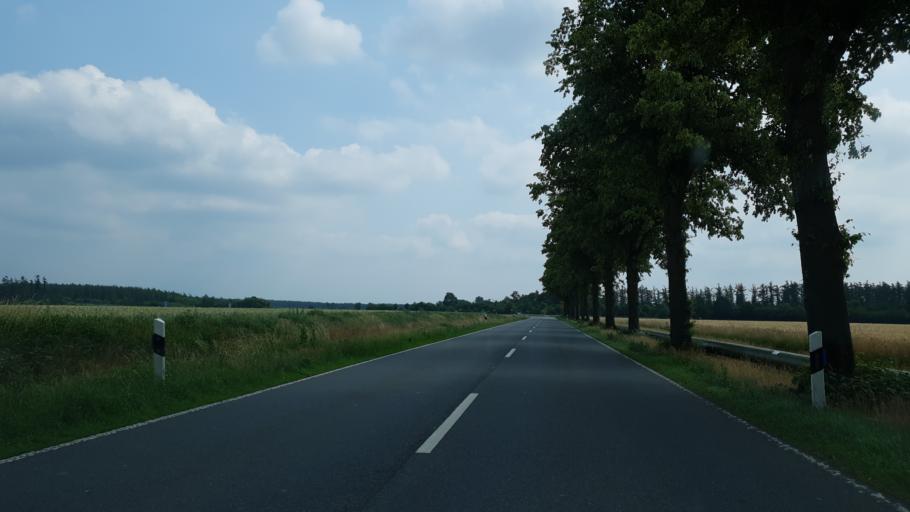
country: DE
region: Lower Saxony
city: Wietmarschen
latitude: 52.5473
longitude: 7.1831
